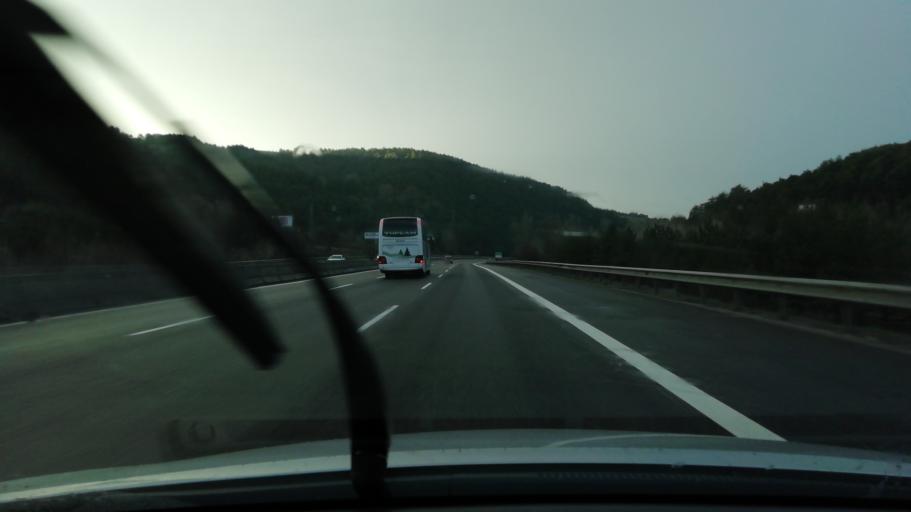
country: TR
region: Bolu
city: Bolu
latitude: 40.7401
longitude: 31.7900
